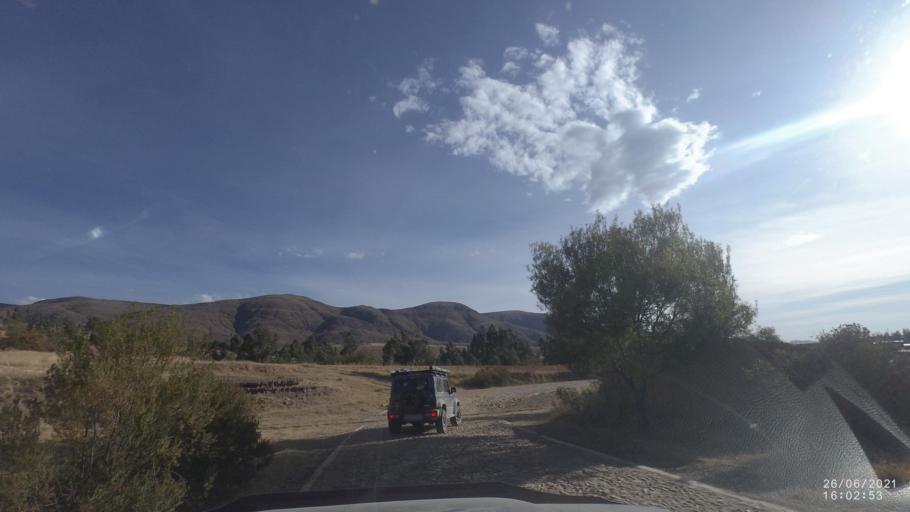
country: BO
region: Cochabamba
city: Arani
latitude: -17.8362
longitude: -65.7494
